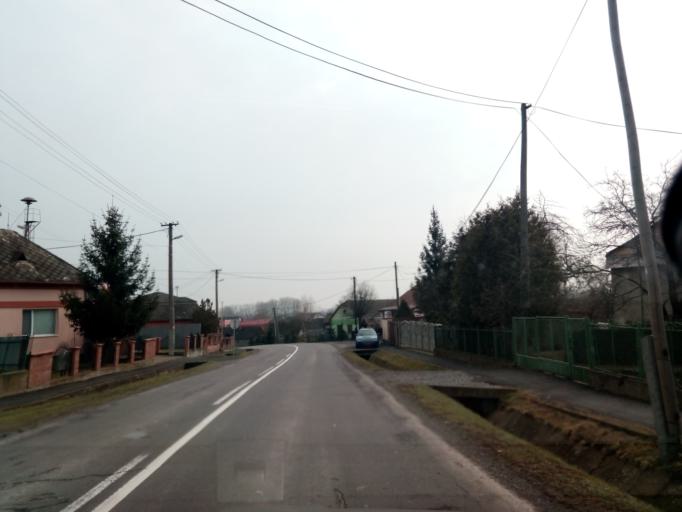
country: SK
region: Kosicky
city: Secovce
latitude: 48.6143
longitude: 21.6061
